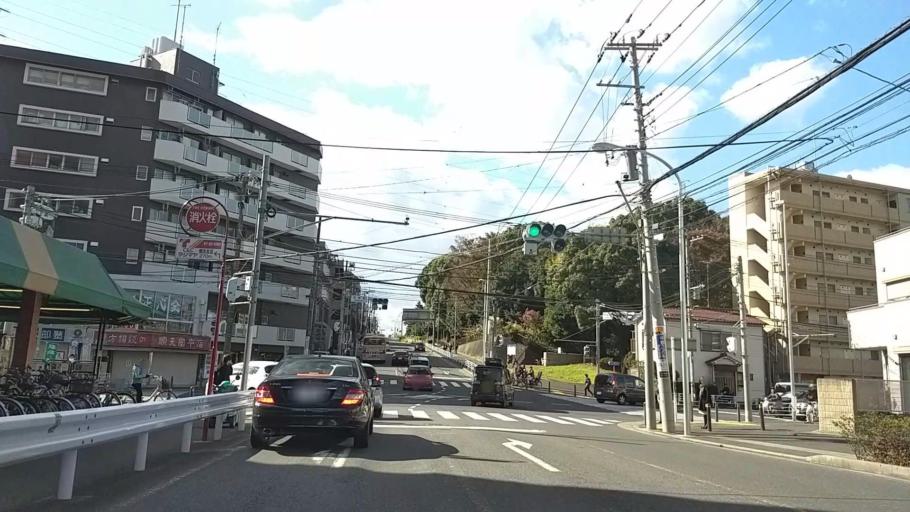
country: JP
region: Kanagawa
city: Yokohama
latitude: 35.4953
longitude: 139.6196
